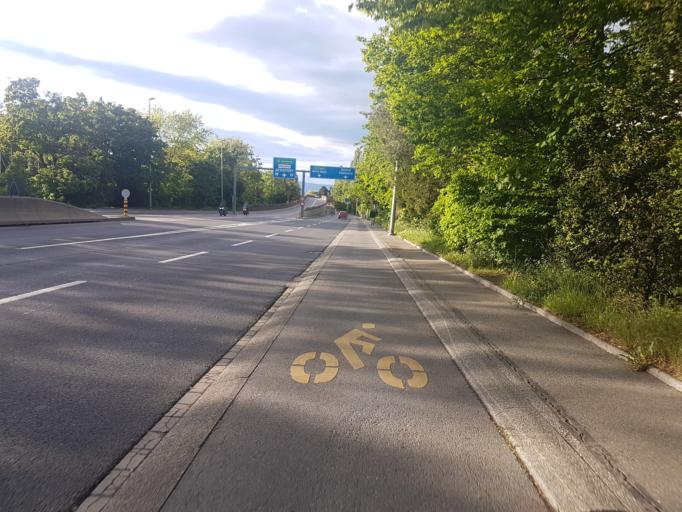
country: CH
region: Geneva
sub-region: Geneva
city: Les Avanchets
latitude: 46.2080
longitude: 6.1099
